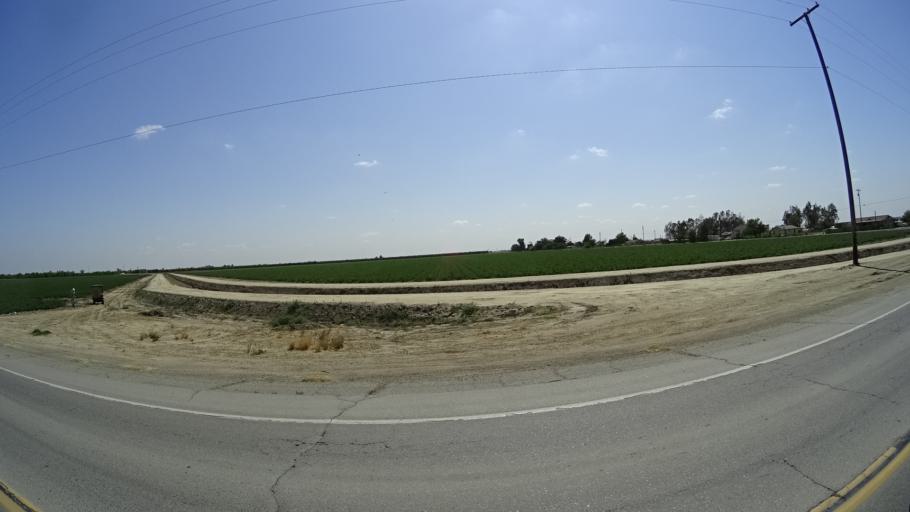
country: US
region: California
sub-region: Kings County
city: Home Garden
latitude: 36.2852
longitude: -119.6370
